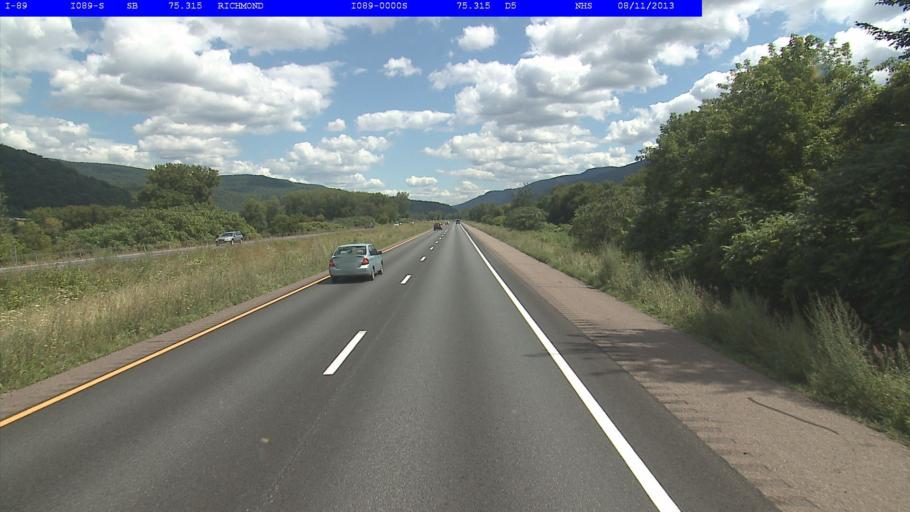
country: US
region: Vermont
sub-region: Chittenden County
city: Williston
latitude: 44.3952
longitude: -72.9678
